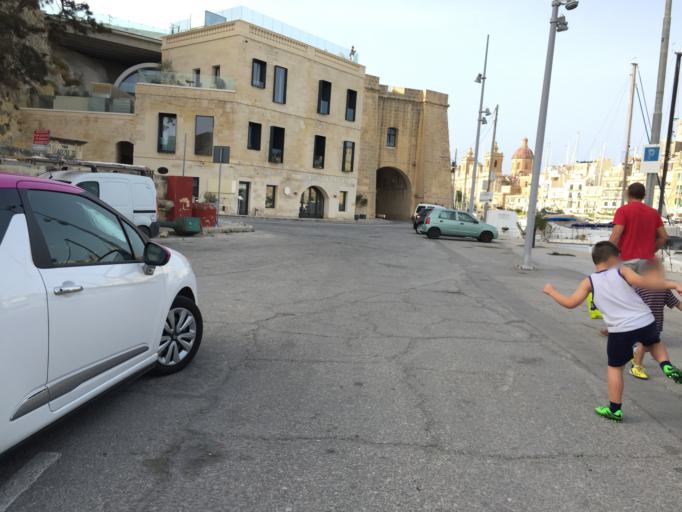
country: MT
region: L-Isla
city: Senglea
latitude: 35.8847
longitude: 14.5198
